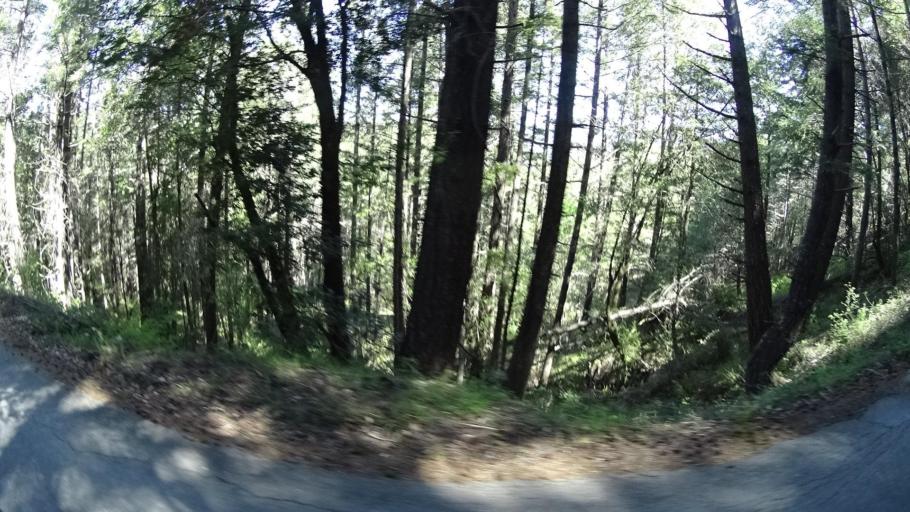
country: US
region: California
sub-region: Humboldt County
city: Rio Dell
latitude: 40.2182
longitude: -124.1099
